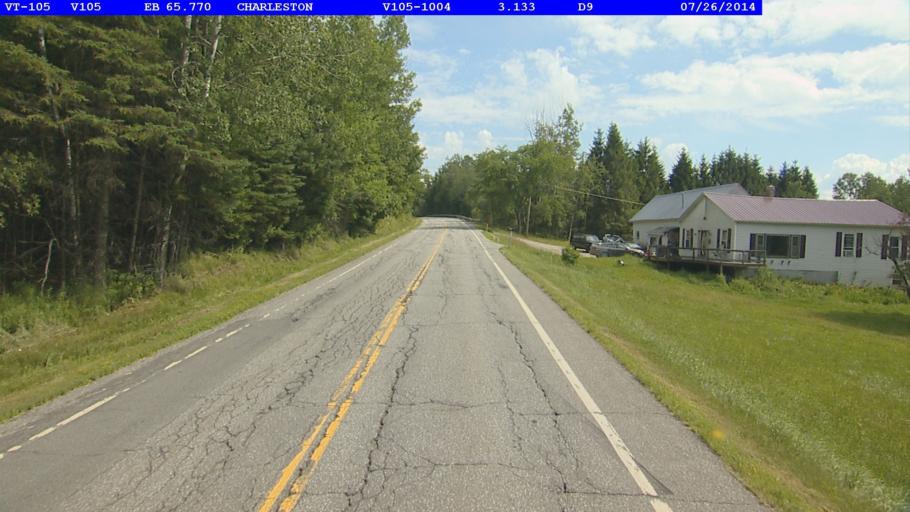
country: US
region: Vermont
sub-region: Orleans County
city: Newport
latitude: 44.8714
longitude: -72.0499
